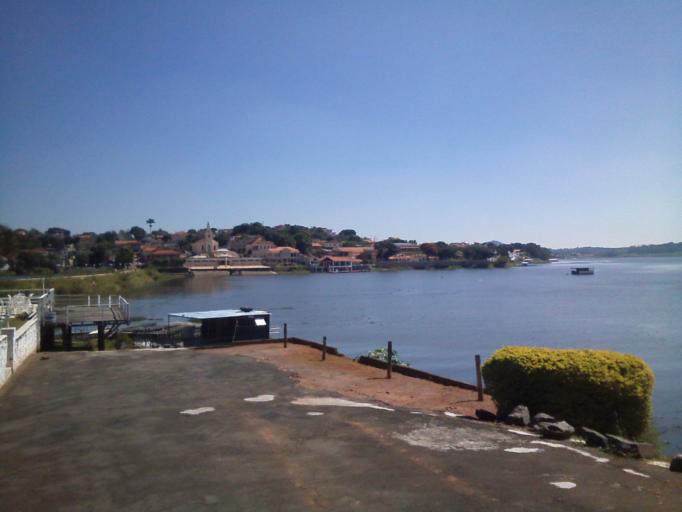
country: BR
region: Minas Gerais
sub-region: Alfenas
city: Alfenas
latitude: -21.4080
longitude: -45.8252
